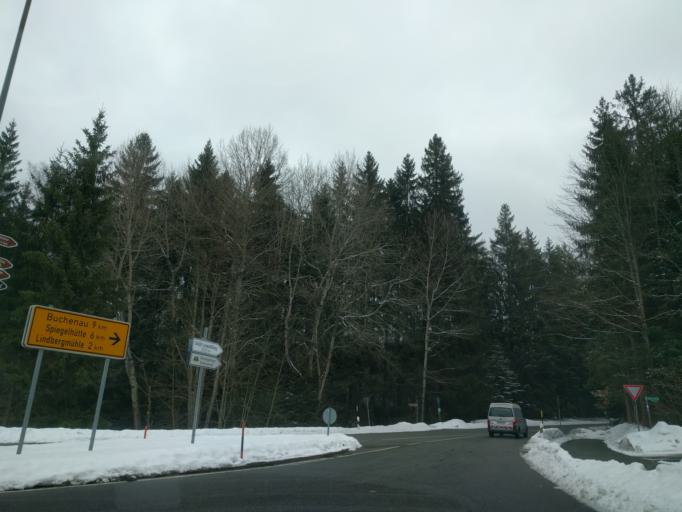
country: DE
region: Bavaria
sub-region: Lower Bavaria
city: Lindberg
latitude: 49.0527
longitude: 13.2380
